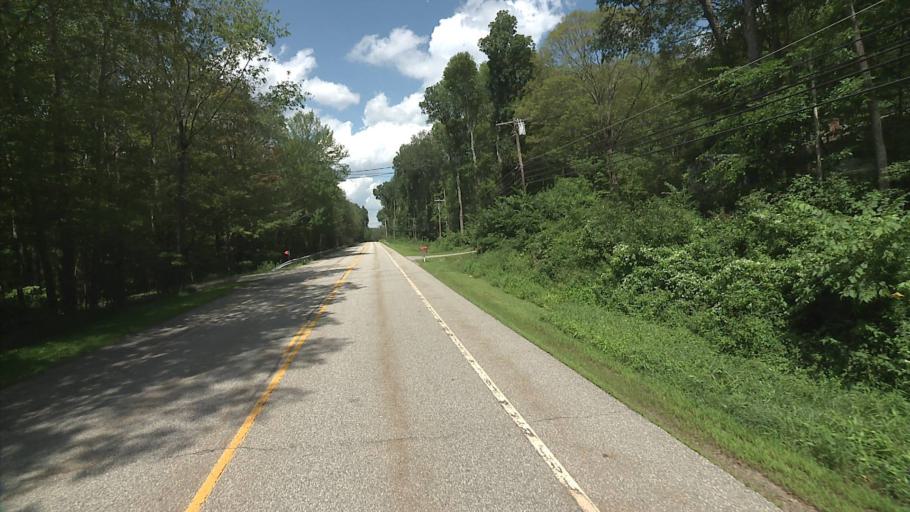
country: US
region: Connecticut
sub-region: Tolland County
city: Storrs
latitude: 41.8505
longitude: -72.1638
